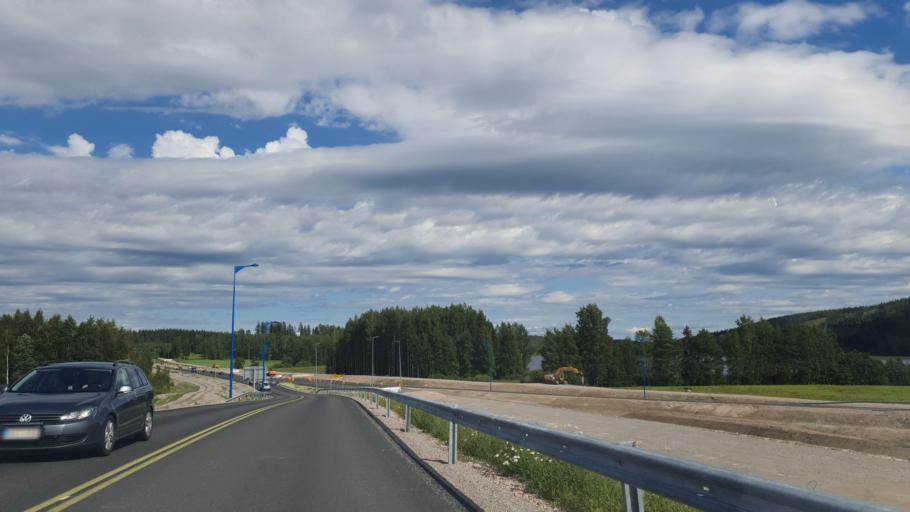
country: FI
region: Central Finland
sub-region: Jaemsae
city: Jaemsae
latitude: 61.8894
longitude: 25.2866
